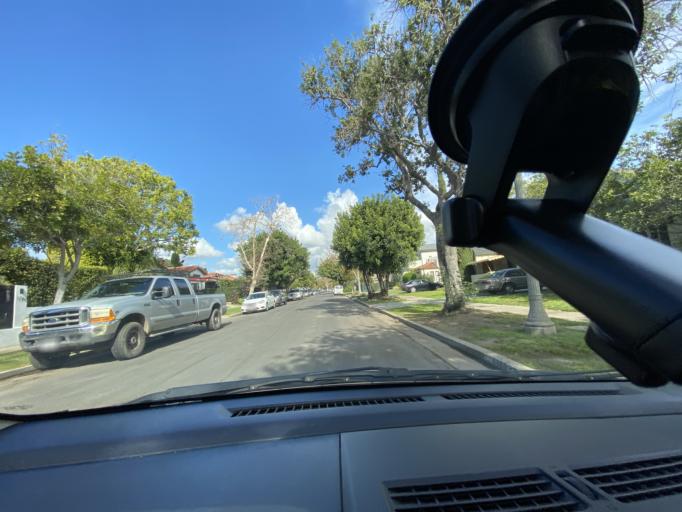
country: US
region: California
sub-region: Los Angeles County
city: Culver City
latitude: 34.0467
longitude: -118.3839
